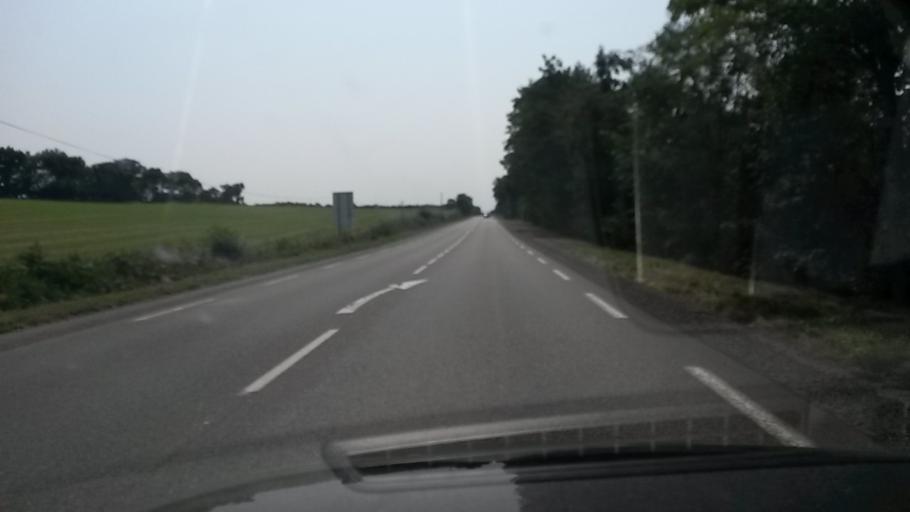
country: FR
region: Pays de la Loire
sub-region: Departement de la Mayenne
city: Chateau-Gontier
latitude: 47.8626
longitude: -0.6903
